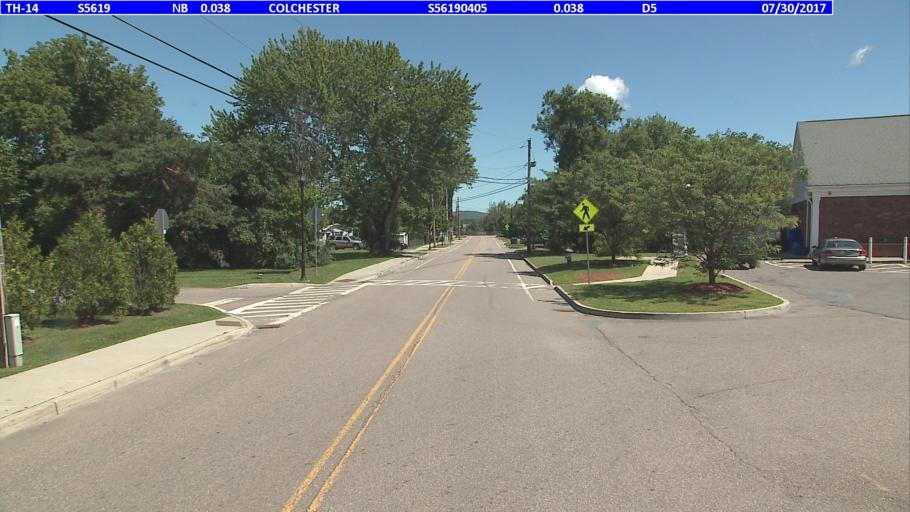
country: US
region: Vermont
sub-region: Chittenden County
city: Winooski
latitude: 44.4977
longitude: -73.1591
